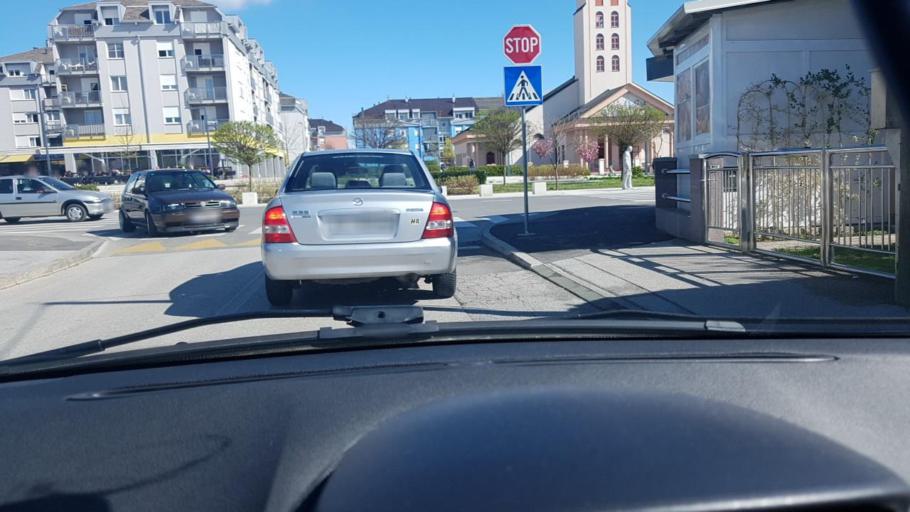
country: HR
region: Zagrebacka
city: Brdovec
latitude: 45.8693
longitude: 15.7956
